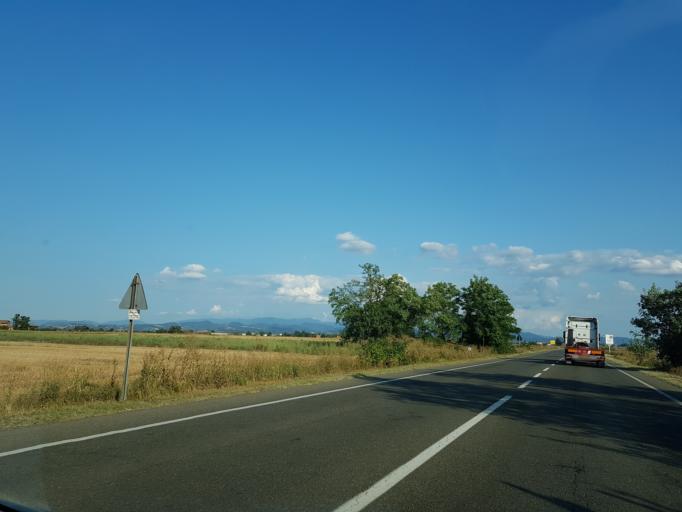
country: IT
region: Piedmont
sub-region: Provincia di Alessandria
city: Pozzolo Formigaro
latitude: 44.8215
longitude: 8.7518
